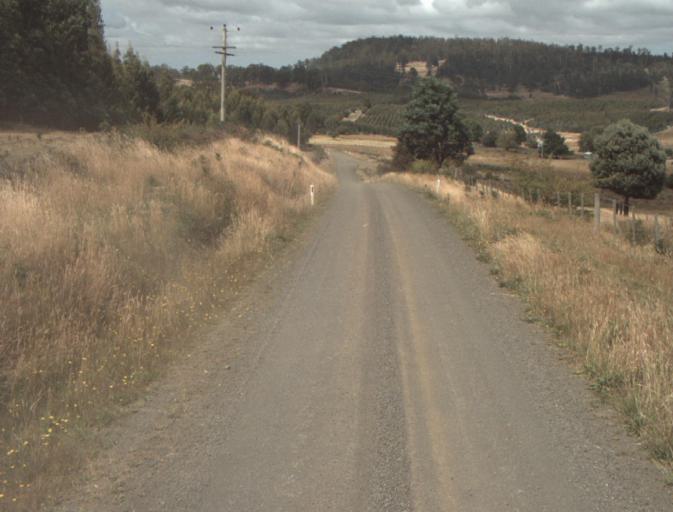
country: AU
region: Tasmania
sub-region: Northern Midlands
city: Evandale
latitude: -41.5223
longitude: 147.4674
